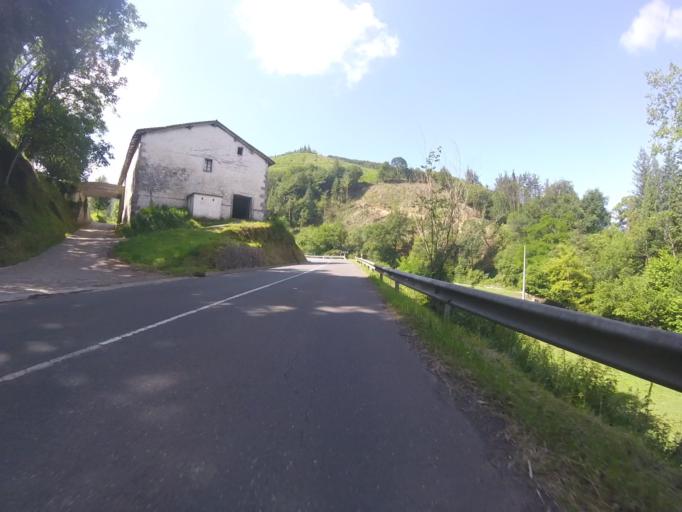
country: ES
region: Basque Country
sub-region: Provincia de Guipuzcoa
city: Azpeitia
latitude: 43.1796
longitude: -2.2252
